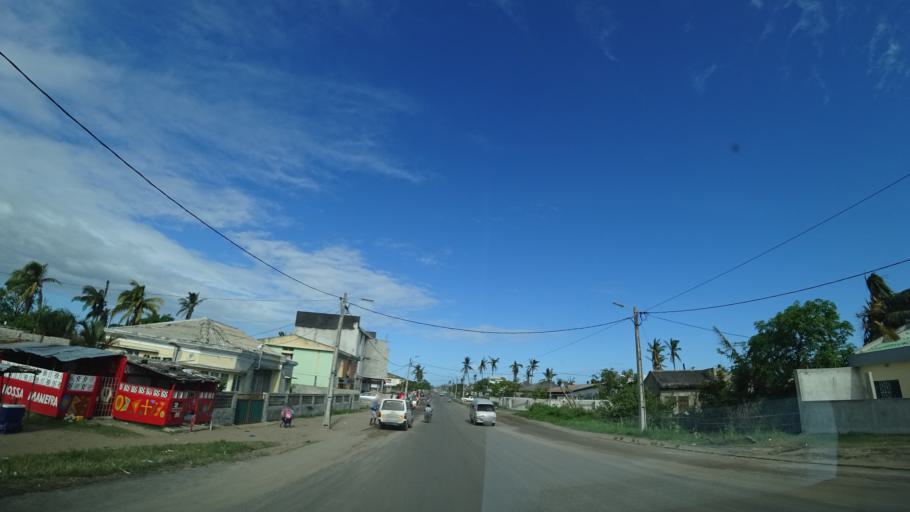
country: MZ
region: Sofala
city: Beira
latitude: -19.7835
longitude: 34.8792
